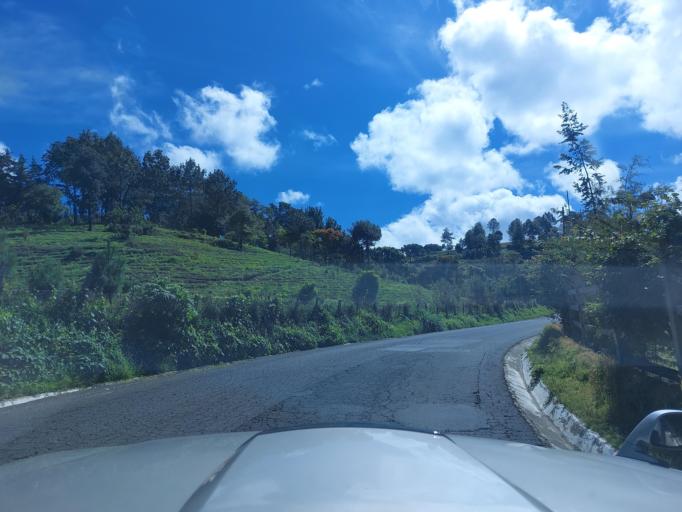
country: GT
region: Chimaltenango
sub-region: Municipio de San Juan Comalapa
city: Comalapa
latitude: 14.7193
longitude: -90.8886
